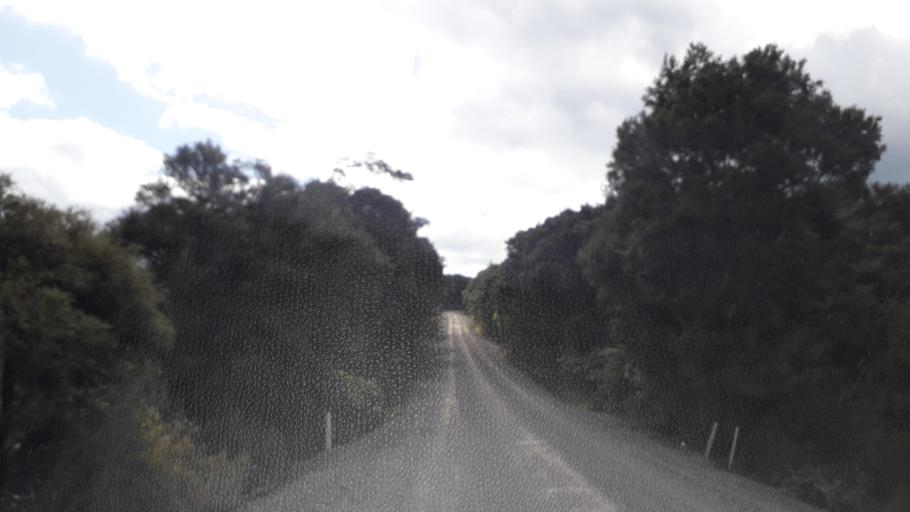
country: NZ
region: Northland
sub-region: Far North District
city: Paihia
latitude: -35.2992
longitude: 174.2188
